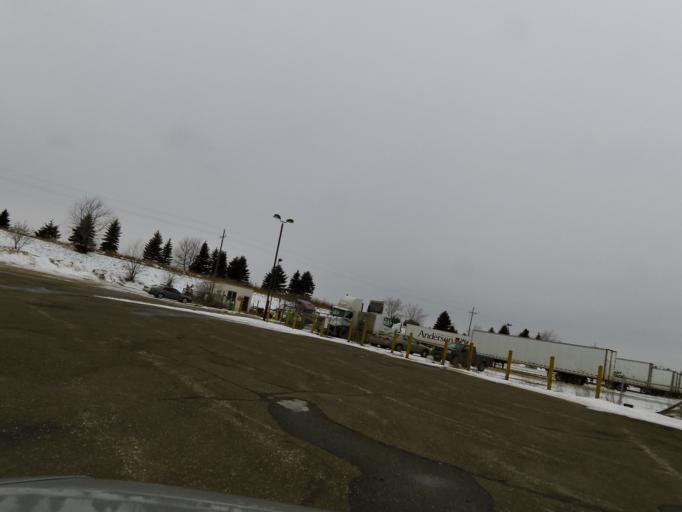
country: US
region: Wisconsin
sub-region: Saint Croix County
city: North Hudson
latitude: 44.9858
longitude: -92.7801
